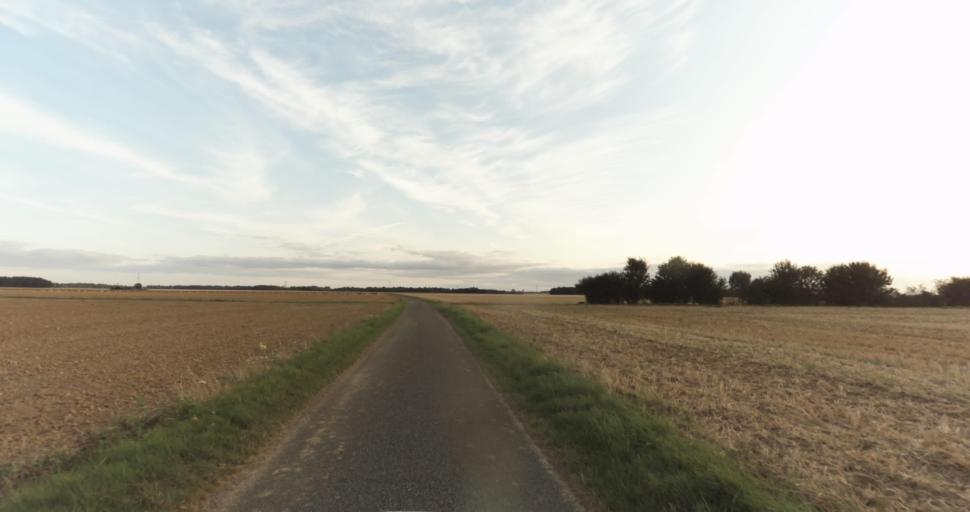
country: FR
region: Haute-Normandie
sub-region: Departement de l'Eure
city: La Madeleine-de-Nonancourt
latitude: 48.8726
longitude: 1.2310
